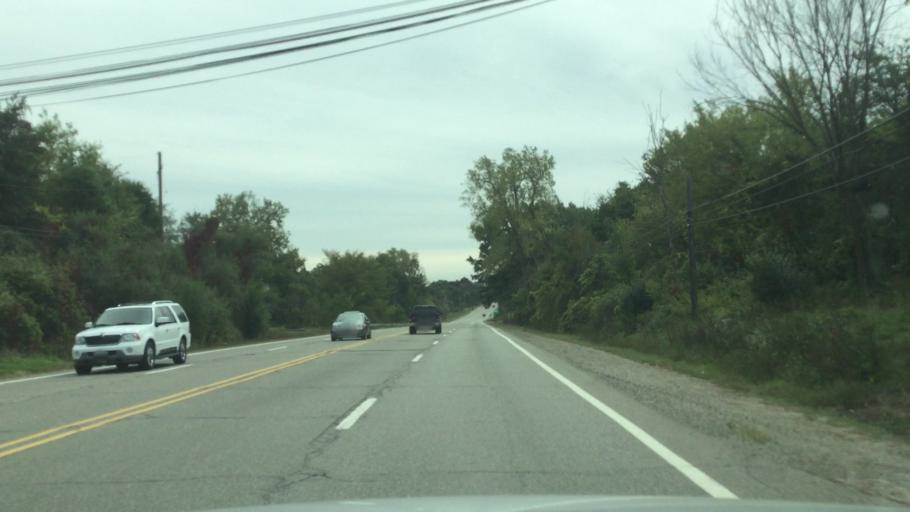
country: US
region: Michigan
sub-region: Oakland County
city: Ortonville
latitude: 42.7840
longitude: -83.5031
